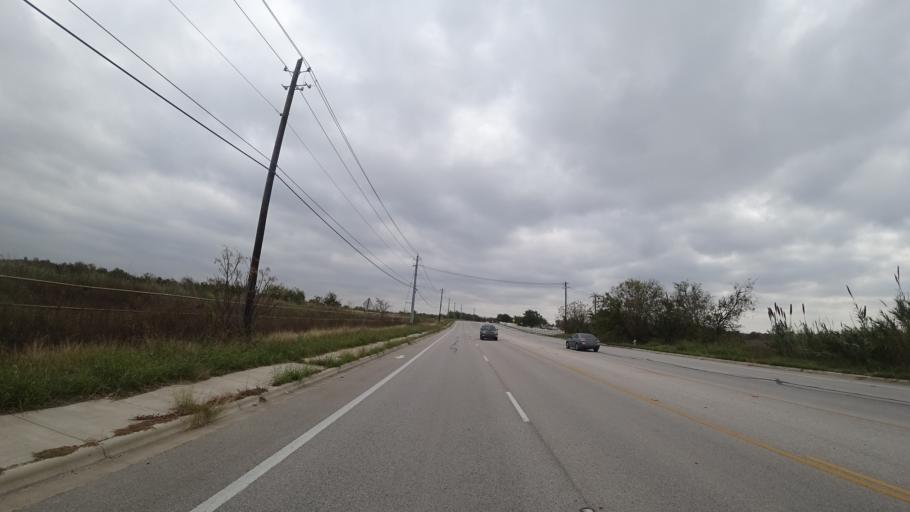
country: US
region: Texas
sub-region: Travis County
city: Pflugerville
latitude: 30.3956
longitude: -97.6312
